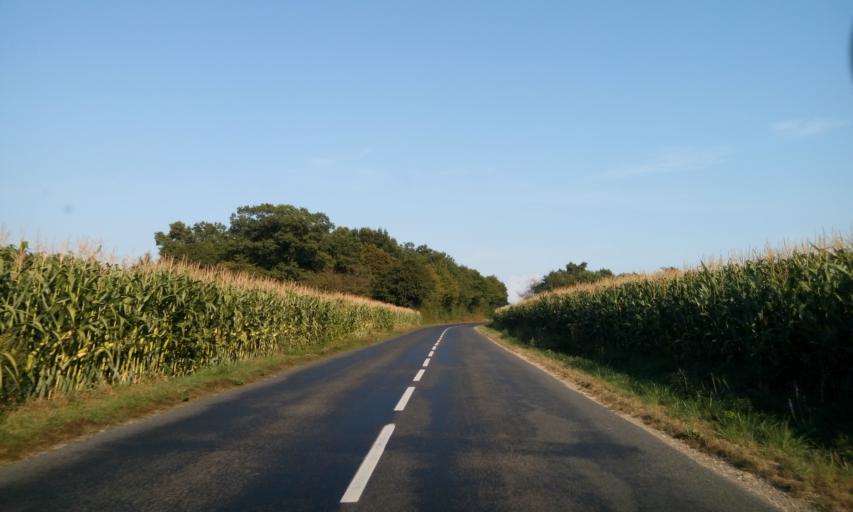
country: FR
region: Rhone-Alpes
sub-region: Departement de l'Ain
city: Amberieux-en-Dombes
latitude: 46.0010
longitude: 4.8787
